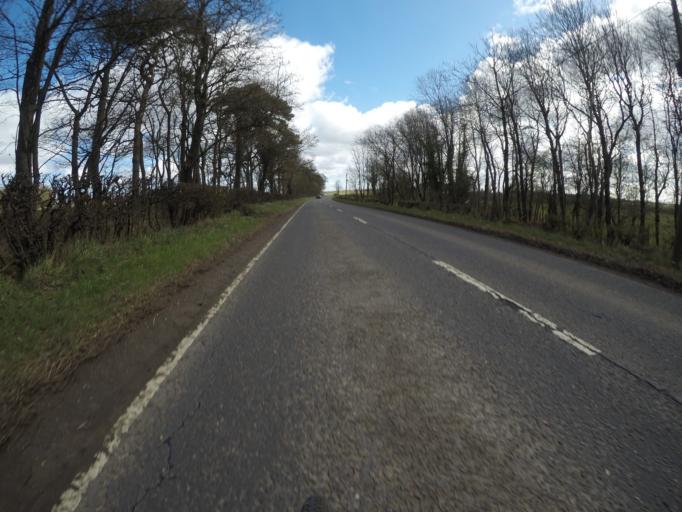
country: GB
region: Scotland
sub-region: South Ayrshire
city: Dundonald
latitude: 55.5870
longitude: -4.5644
